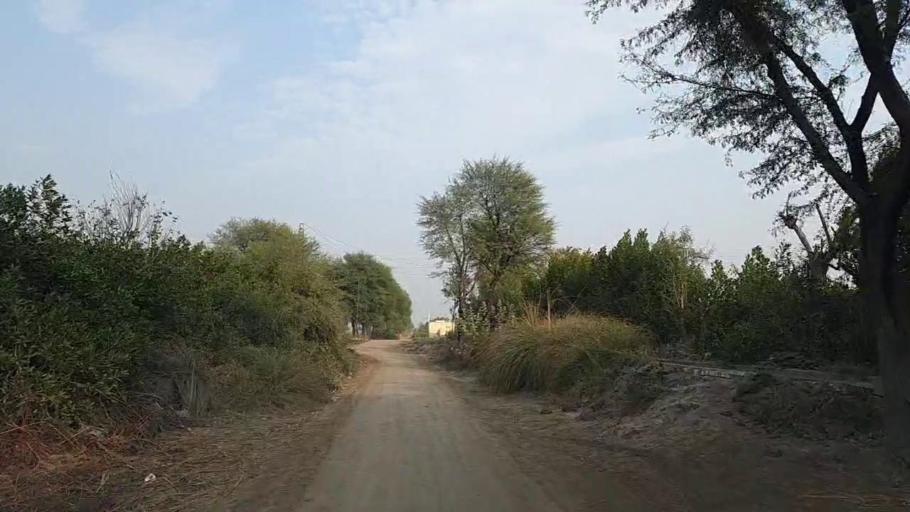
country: PK
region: Sindh
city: Jam Sahib
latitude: 26.3098
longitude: 68.5367
